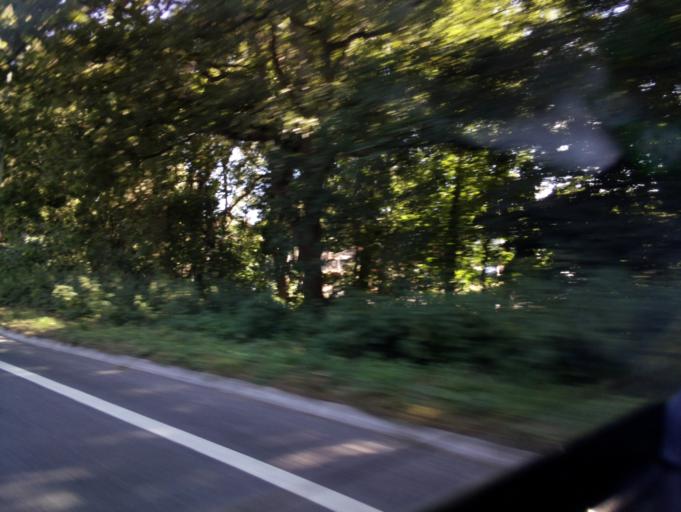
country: GB
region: England
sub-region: Bournemouth
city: Bournemouth
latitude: 50.7653
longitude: -1.8825
